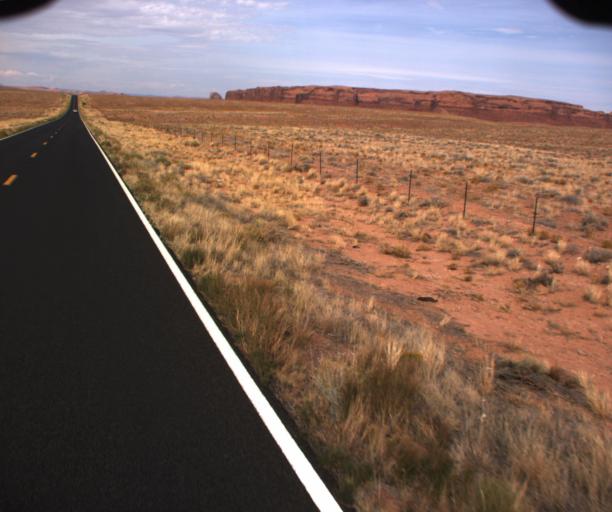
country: US
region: Arizona
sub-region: Apache County
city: Many Farms
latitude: 36.5759
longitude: -109.5513
